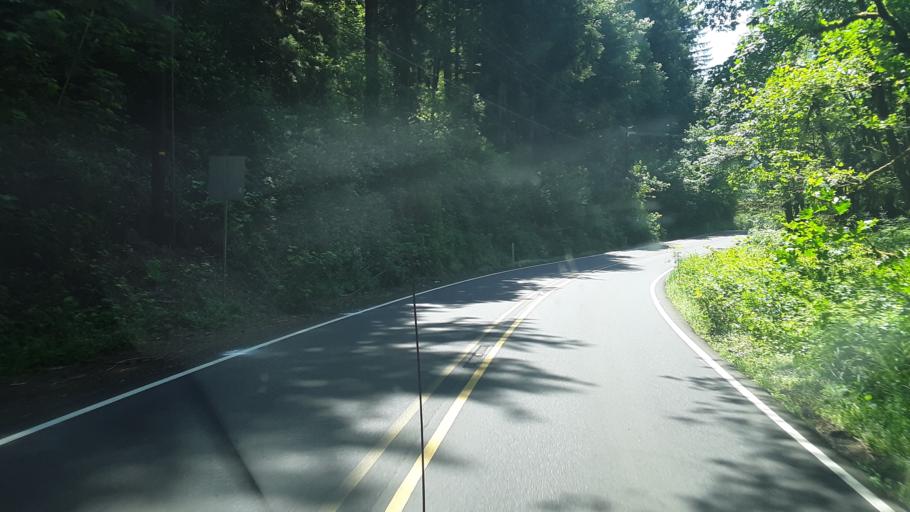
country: US
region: Washington
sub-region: Clark County
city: Amboy
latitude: 45.9357
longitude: -122.3796
